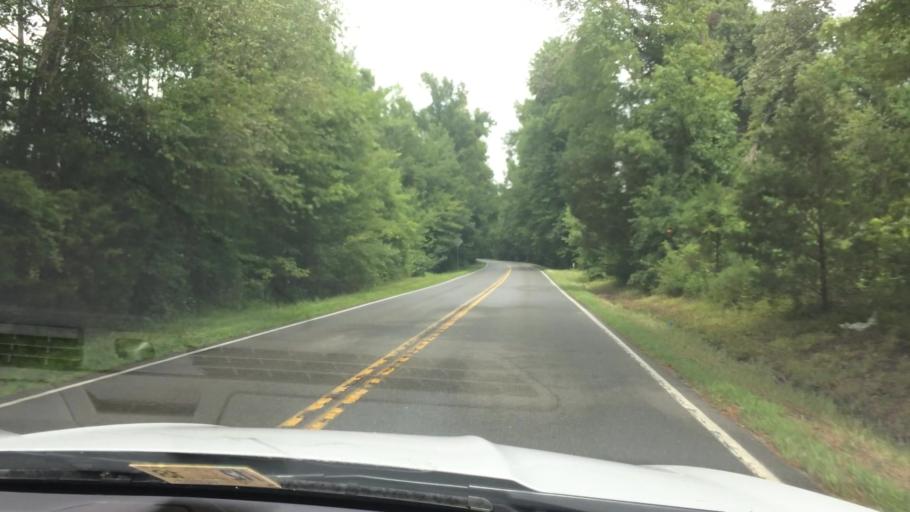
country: US
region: Virginia
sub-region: Charles City County
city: Charles City
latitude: 37.4229
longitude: -77.0404
